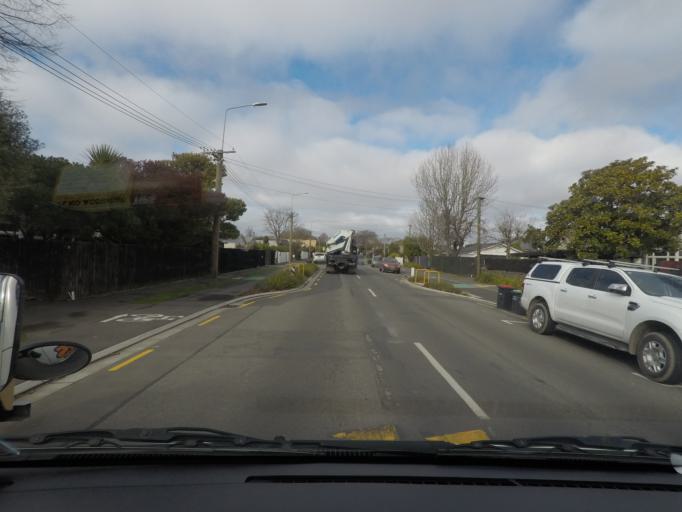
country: NZ
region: Canterbury
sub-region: Christchurch City
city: Christchurch
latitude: -43.5070
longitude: 172.6293
